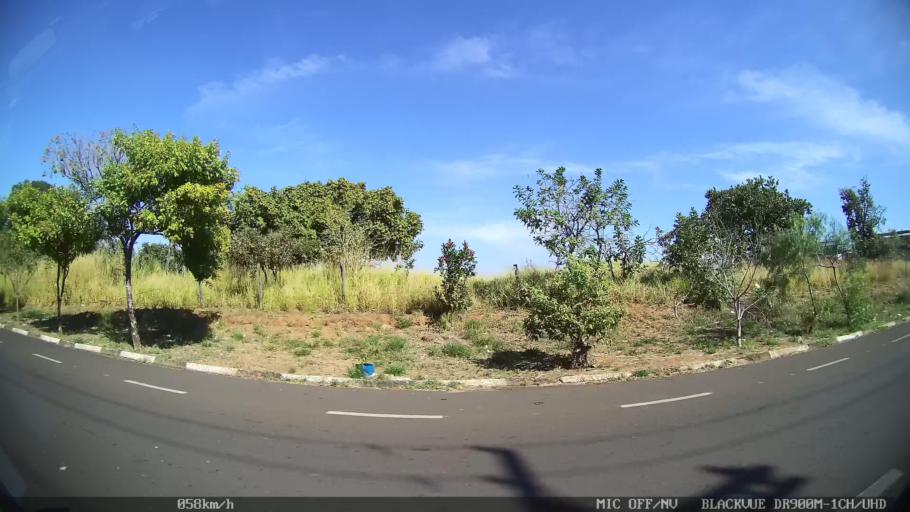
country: BR
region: Sao Paulo
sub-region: Franca
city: Franca
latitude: -20.5485
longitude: -47.4527
